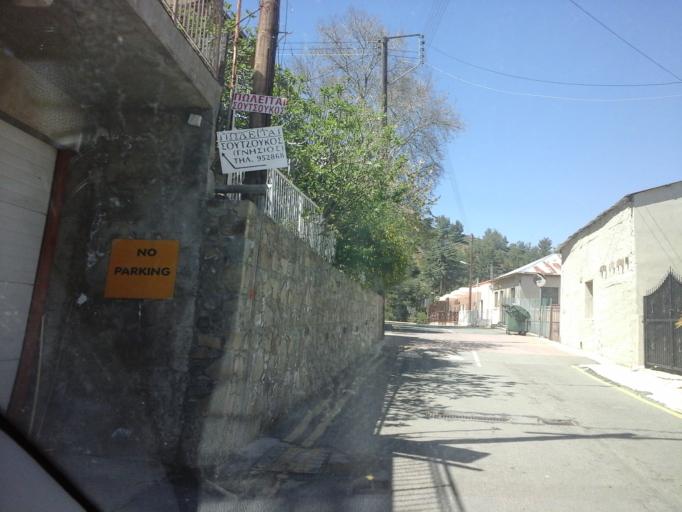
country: CY
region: Lefkosia
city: Kakopetria
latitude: 35.0010
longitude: 32.8043
